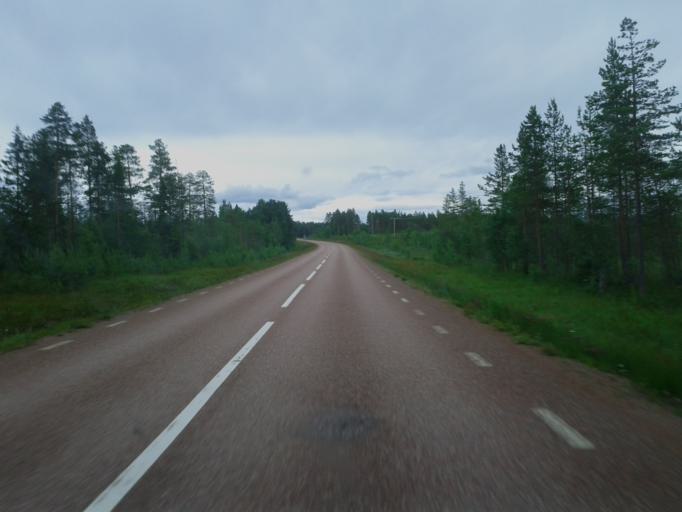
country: SE
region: Dalarna
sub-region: Alvdalens Kommun
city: AElvdalen
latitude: 61.5355
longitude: 13.3475
